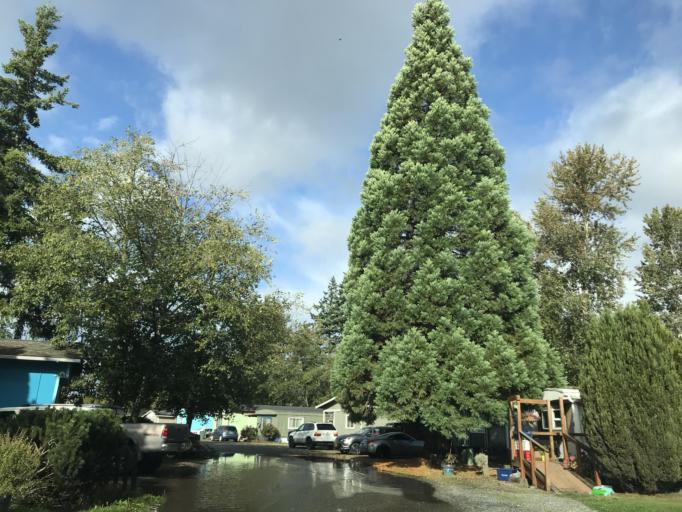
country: US
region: Washington
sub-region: Whatcom County
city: Bellingham
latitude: 48.7876
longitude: -122.4979
